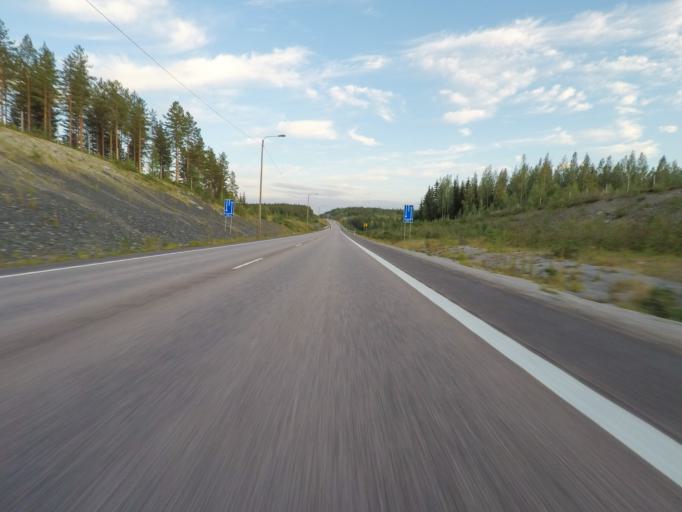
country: FI
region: Central Finland
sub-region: Jyvaeskylae
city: Toivakka
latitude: 62.1054
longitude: 25.9800
